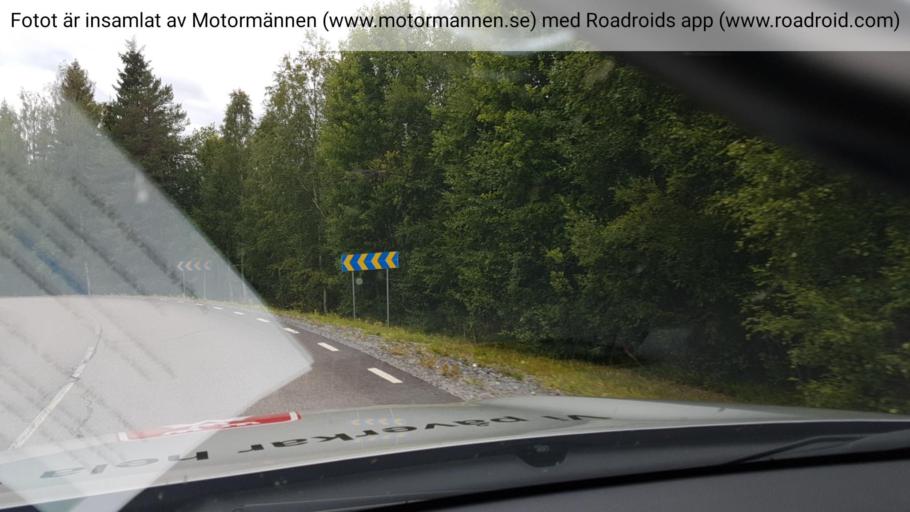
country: SE
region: Norrbotten
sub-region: Lulea Kommun
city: Gammelstad
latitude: 65.6601
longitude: 22.0561
